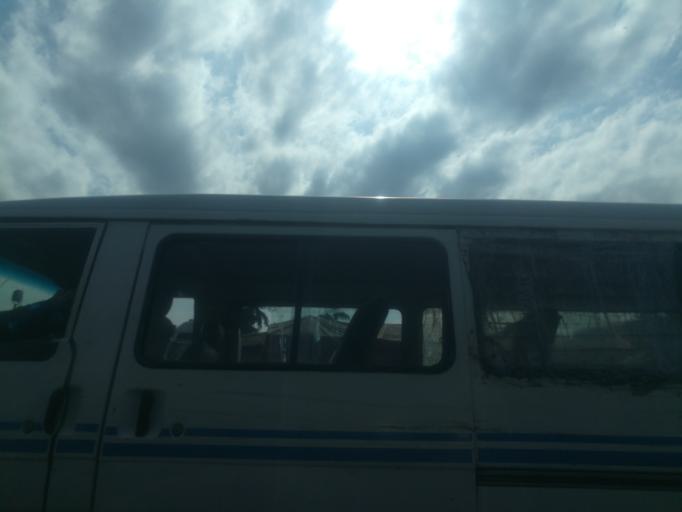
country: NG
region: Oyo
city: Ibadan
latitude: 7.3886
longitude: 3.9354
